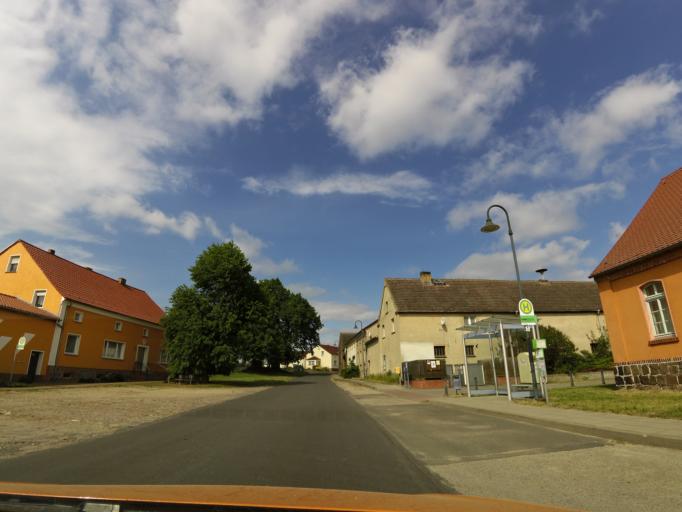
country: DE
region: Brandenburg
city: Wiesenburg
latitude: 52.0768
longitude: 12.5227
